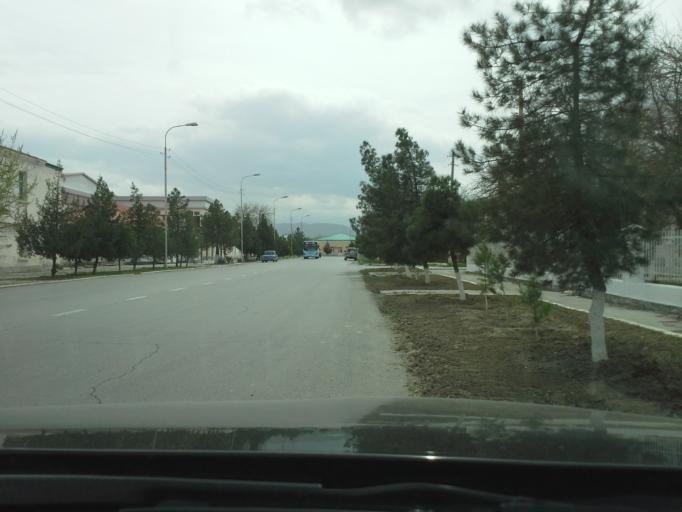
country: TM
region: Ahal
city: Abadan
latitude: 38.0608
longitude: 58.1545
